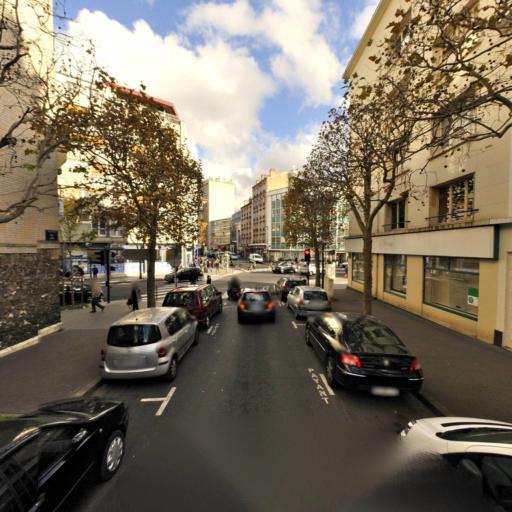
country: FR
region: Ile-de-France
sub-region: Departement des Hauts-de-Seine
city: Boulogne-Billancourt
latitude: 48.8290
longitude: 2.2458
